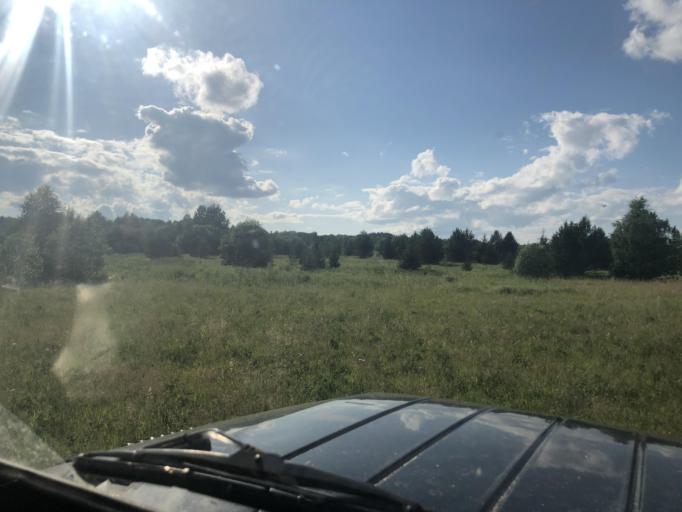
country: RU
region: Komi Republic
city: Vizinga
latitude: 61.2529
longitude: 50.5507
